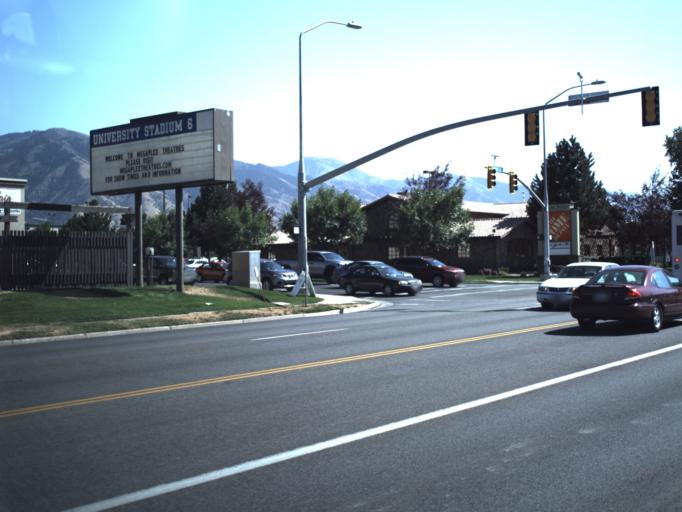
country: US
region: Utah
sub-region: Cache County
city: Logan
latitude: 41.7548
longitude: -111.8345
